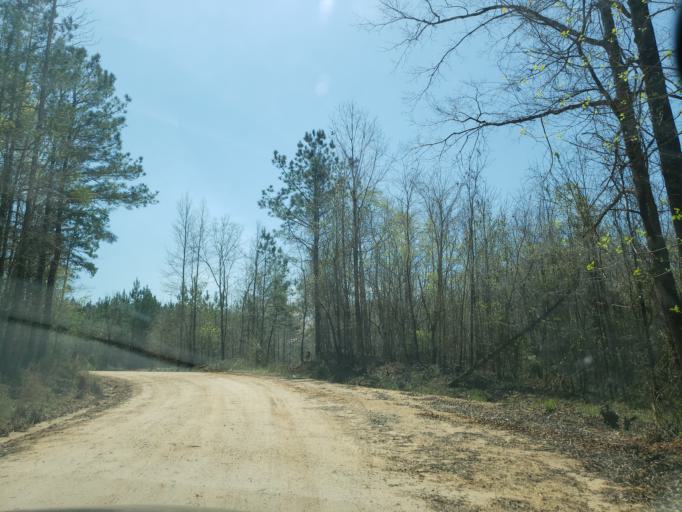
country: US
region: Alabama
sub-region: Tallapoosa County
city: Camp Hill
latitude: 32.6564
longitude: -85.6622
